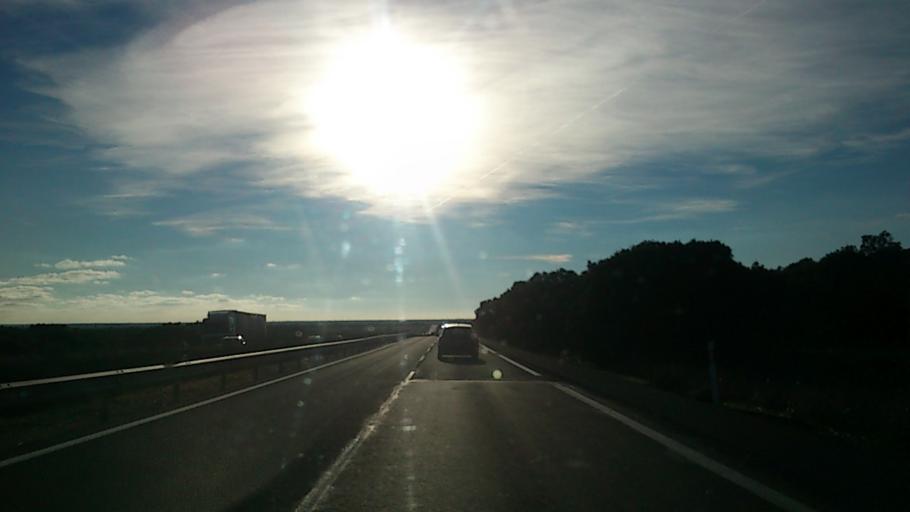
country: ES
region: Castille-La Mancha
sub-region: Provincia de Guadalajara
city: Algora
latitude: 40.9504
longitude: -2.6864
